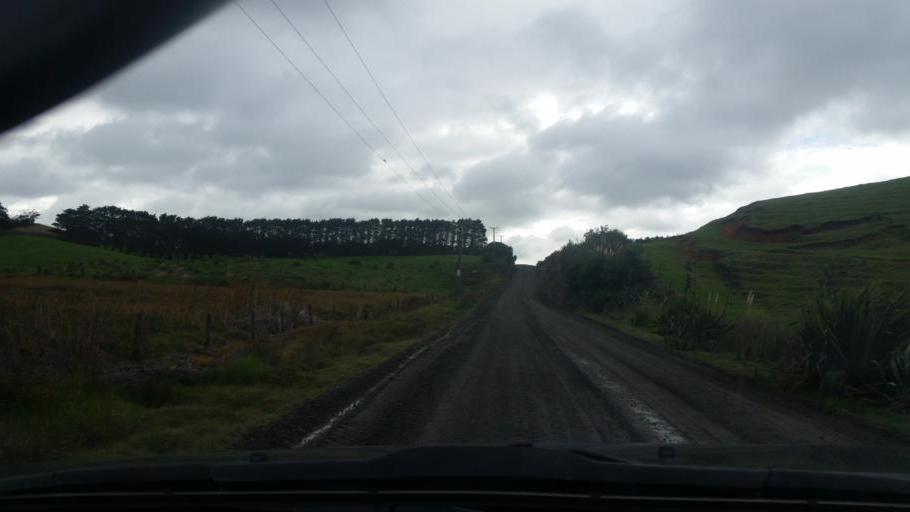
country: NZ
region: Northland
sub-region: Kaipara District
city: Dargaville
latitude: -35.8508
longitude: 173.6635
